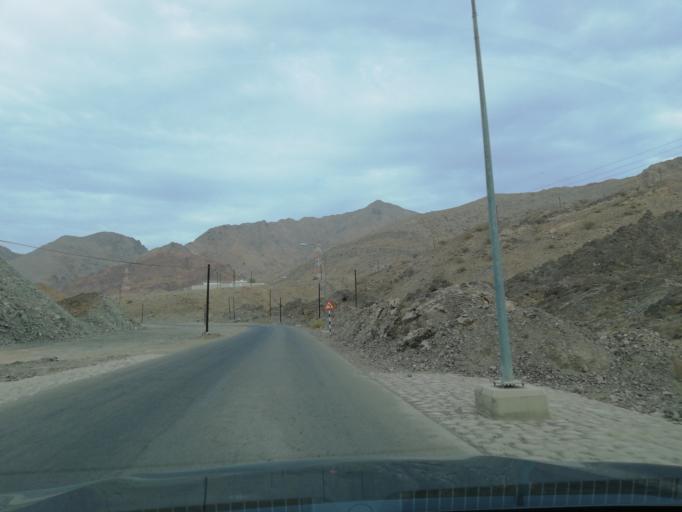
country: OM
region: Muhafazat Masqat
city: Bawshar
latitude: 23.4854
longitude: 58.3396
